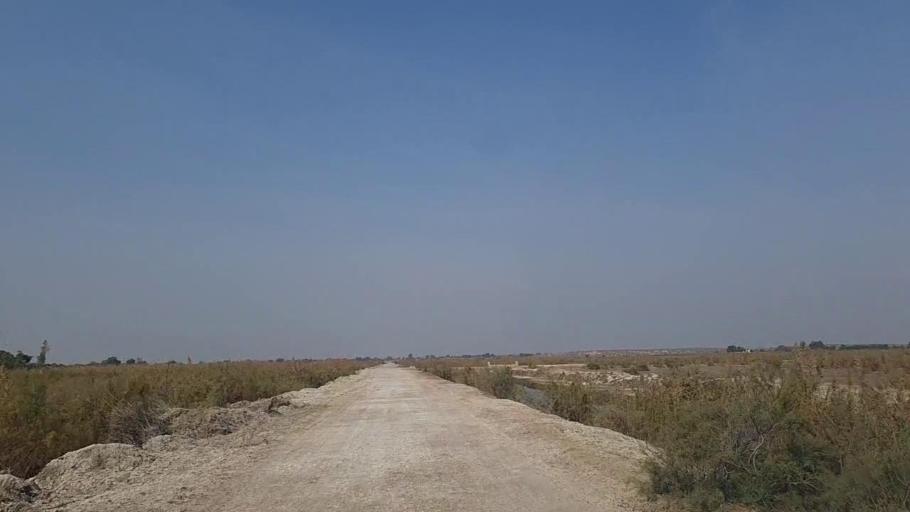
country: PK
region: Sindh
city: Daur
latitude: 26.5001
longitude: 68.4796
